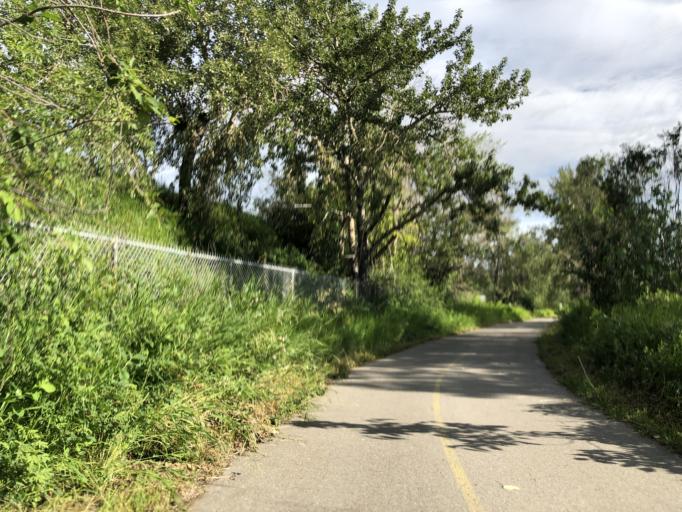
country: CA
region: Alberta
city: Calgary
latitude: 51.0164
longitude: -114.0128
